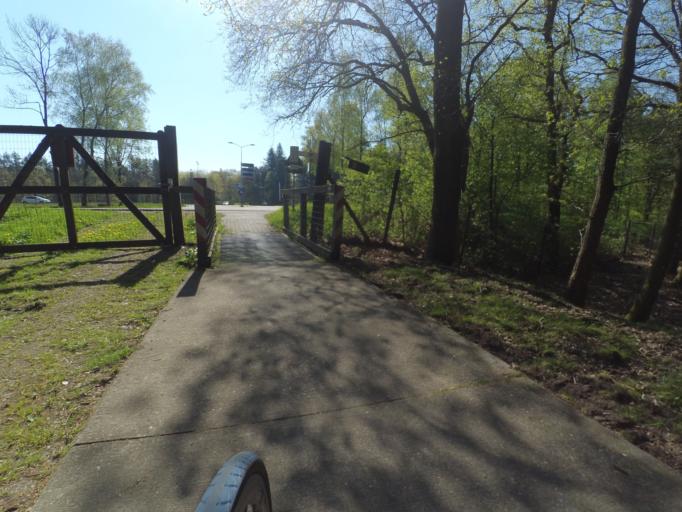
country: NL
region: Gelderland
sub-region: Gemeente Apeldoorn
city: Beekbergen
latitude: 52.1710
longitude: 5.9075
